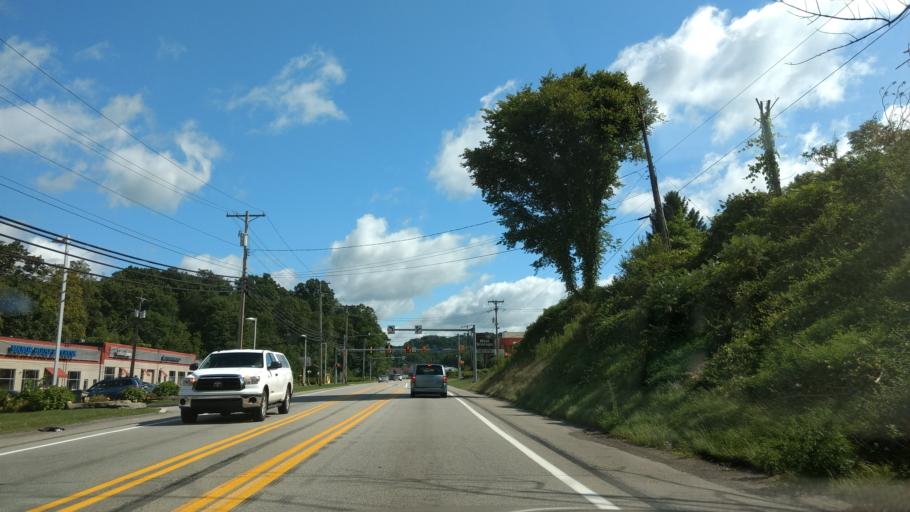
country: US
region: Pennsylvania
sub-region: Westmoreland County
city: Murrysville
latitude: 40.4570
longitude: -79.7092
